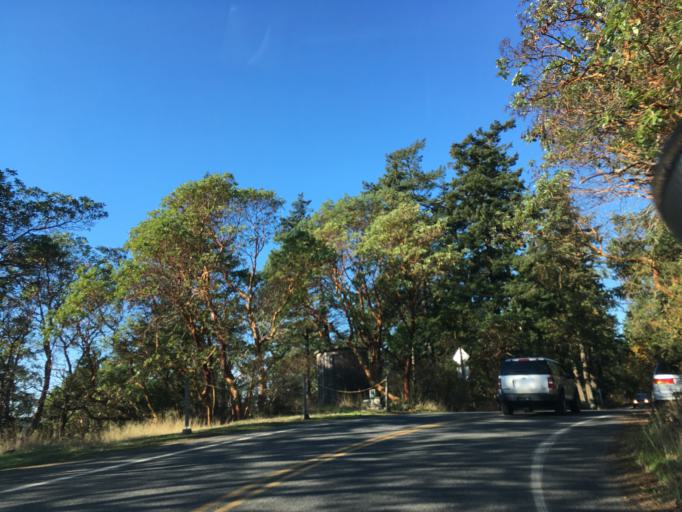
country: US
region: Washington
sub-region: San Juan County
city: Friday Harbor
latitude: 48.5978
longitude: -122.9460
